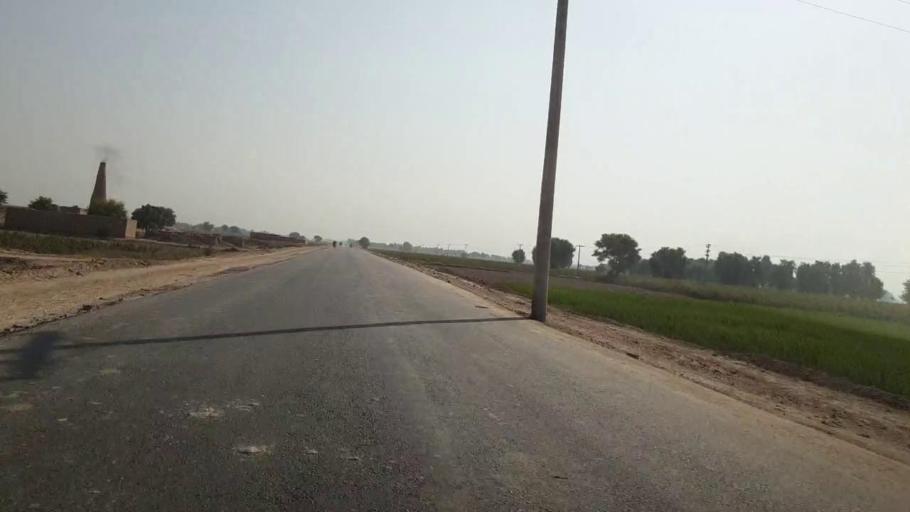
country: PK
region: Sindh
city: Dadu
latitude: 26.6612
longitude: 67.7764
